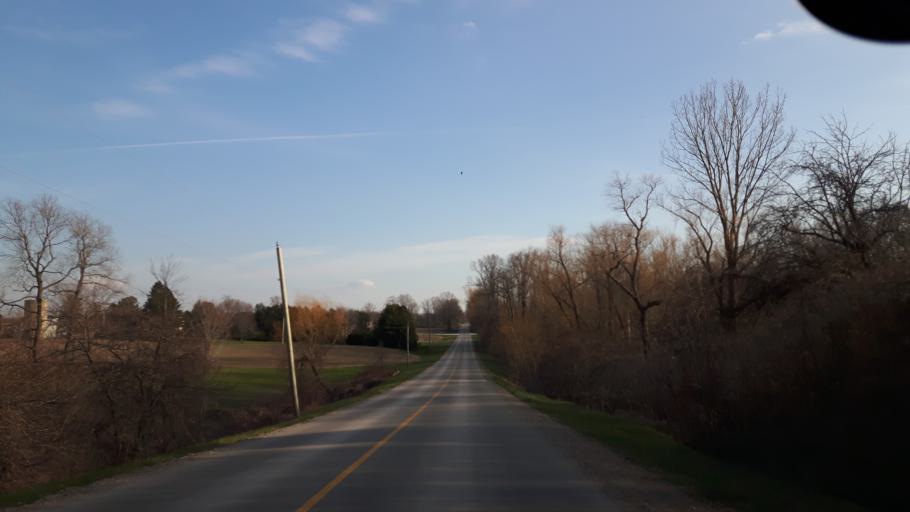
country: CA
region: Ontario
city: Goderich
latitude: 43.6836
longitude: -81.6644
